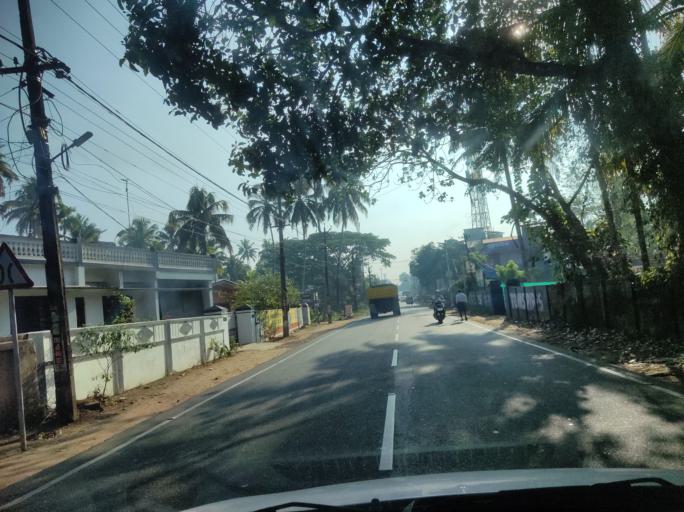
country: IN
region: Kerala
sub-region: Alappuzha
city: Kayankulam
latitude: 9.1769
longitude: 76.5252
